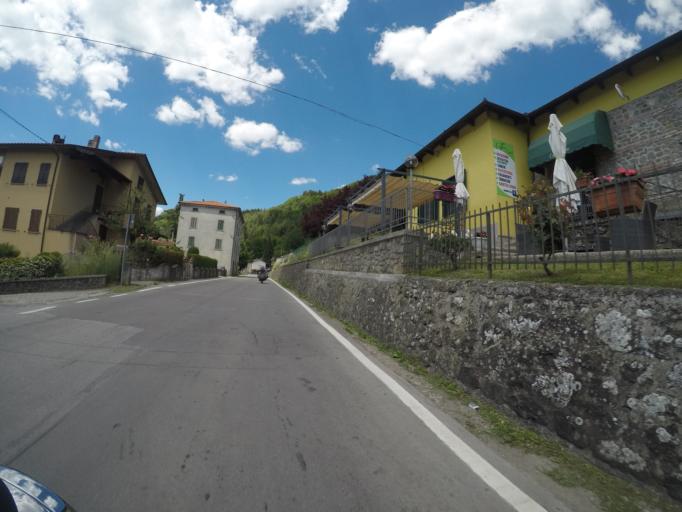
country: IT
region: Tuscany
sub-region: Provincia di Lucca
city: San Romano in Garfagnana
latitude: 44.1627
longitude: 10.3545
